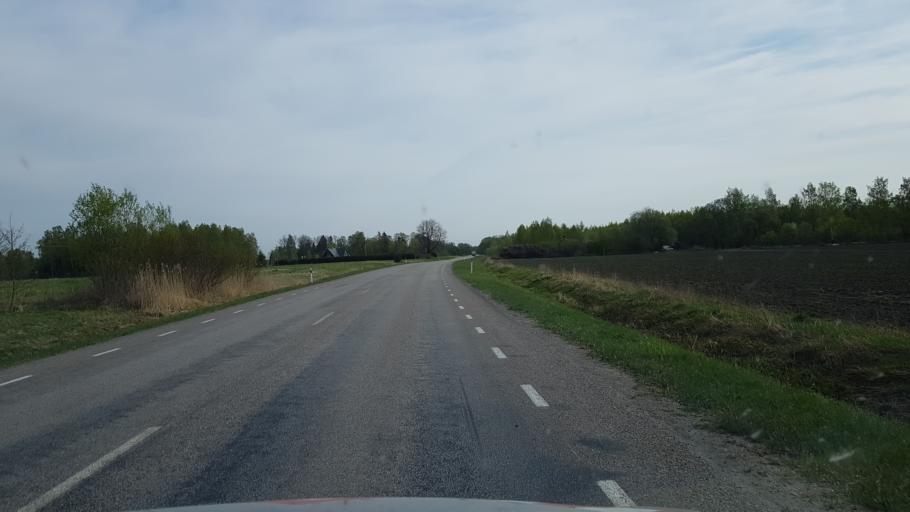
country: EE
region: Paernumaa
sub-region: Audru vald
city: Audru
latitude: 58.3948
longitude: 24.2842
